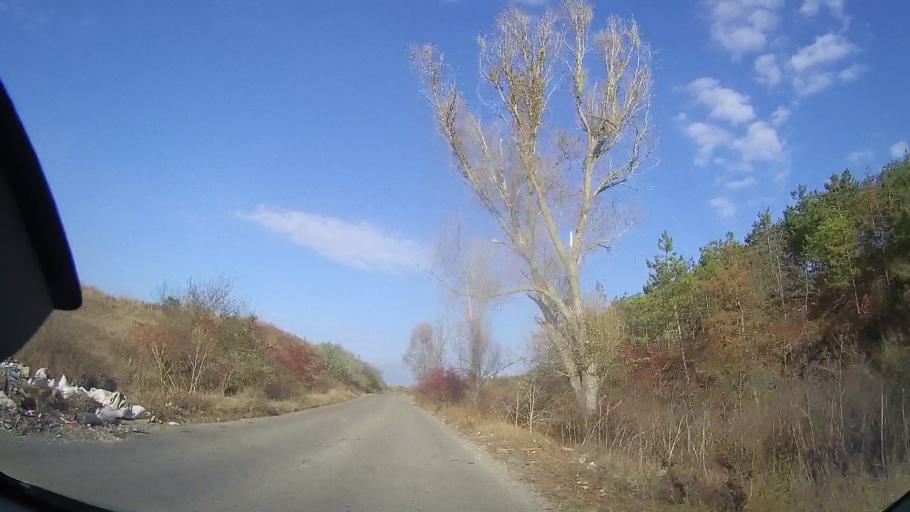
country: RO
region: Constanta
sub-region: Comuna Limanu
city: Limanu
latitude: 43.8204
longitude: 28.5207
